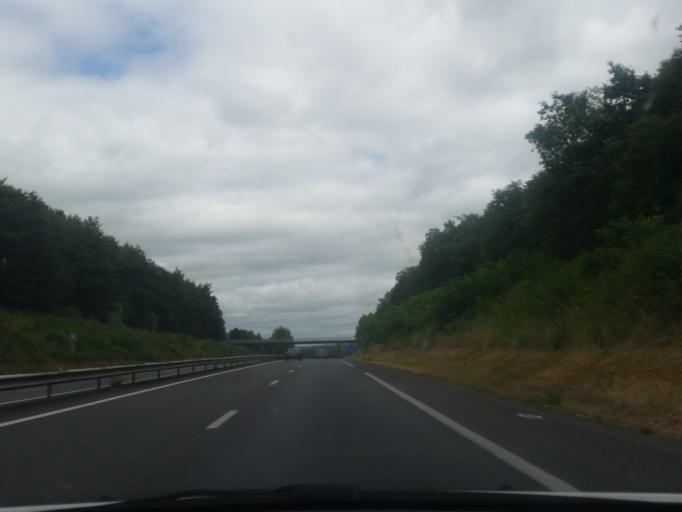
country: FR
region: Pays de la Loire
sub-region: Departement de Maine-et-Loire
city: Seiches-sur-le-Loir
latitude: 47.6057
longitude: -0.3034
